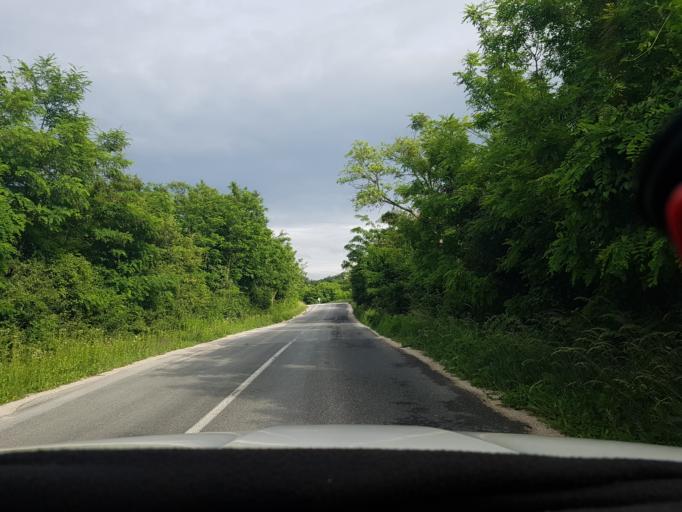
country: HU
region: Komarom-Esztergom
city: Nyergesujfalu
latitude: 47.7265
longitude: 18.5358
